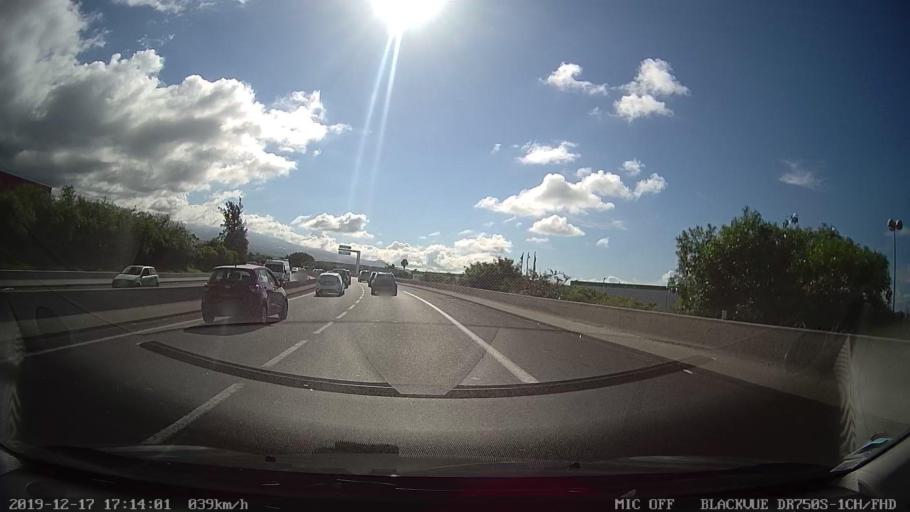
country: RE
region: Reunion
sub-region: Reunion
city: Saint-Louis
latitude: -21.2923
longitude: 55.4040
